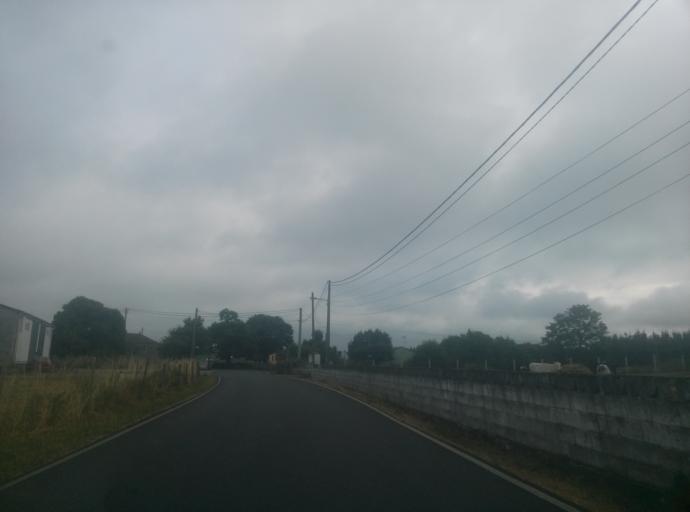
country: ES
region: Galicia
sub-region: Provincia de Lugo
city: Lugo
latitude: 43.0691
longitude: -7.5577
